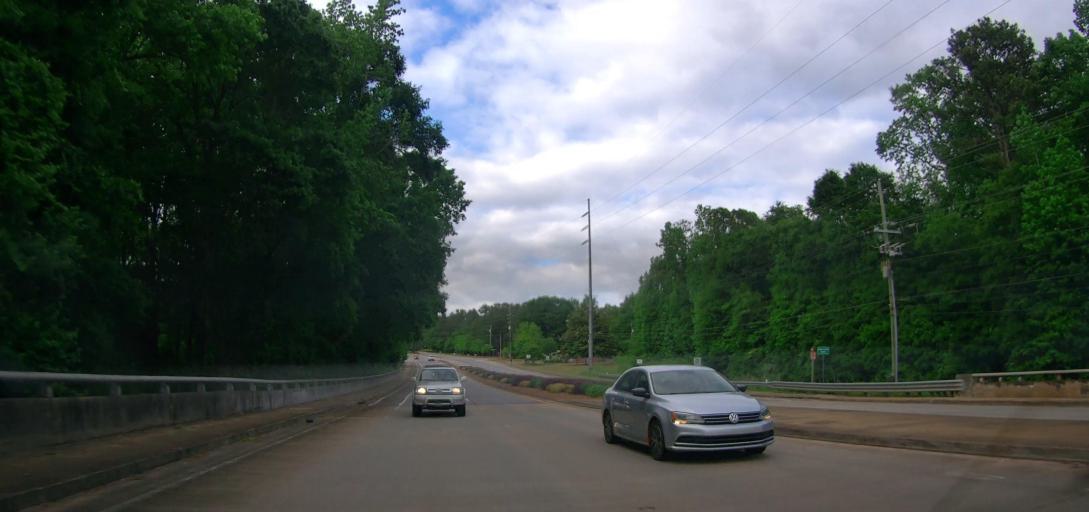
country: US
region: Georgia
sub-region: Oconee County
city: Watkinsville
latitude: 33.9232
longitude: -83.4402
